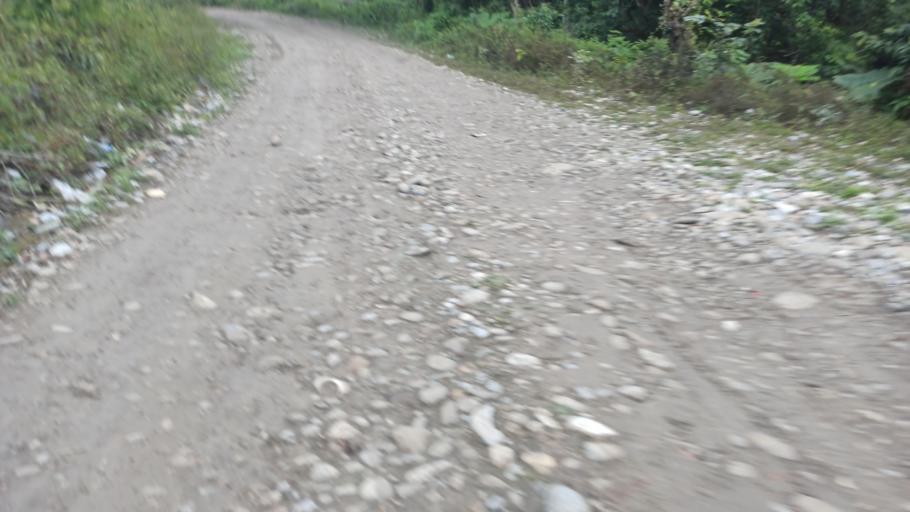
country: MX
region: Veracruz
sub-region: Coatzintla
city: Manuel Maria Contreras
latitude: 20.3509
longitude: -97.4684
